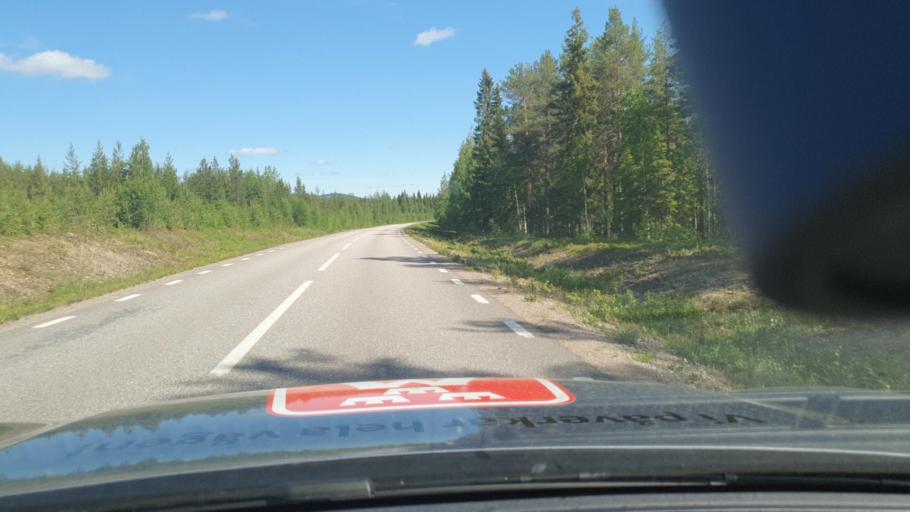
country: SE
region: Norrbotten
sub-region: Overkalix Kommun
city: OEverkalix
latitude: 66.7533
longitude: 22.6729
